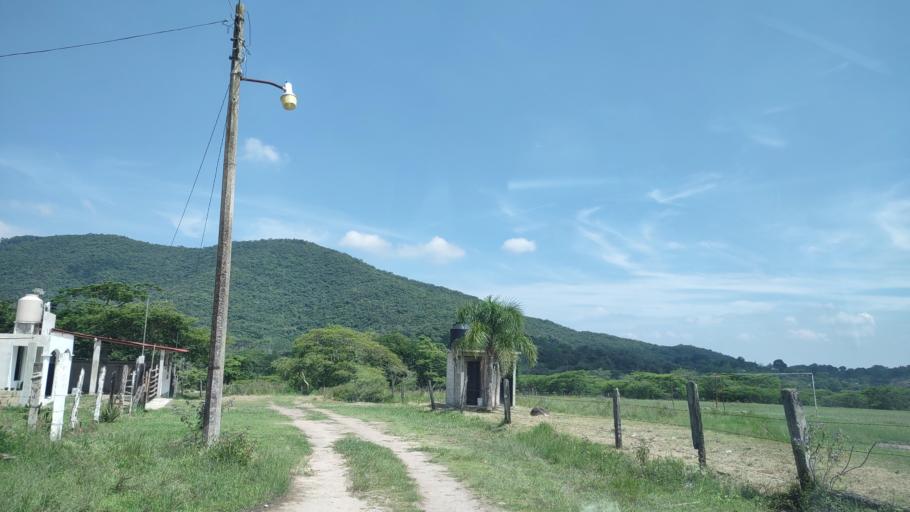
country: MX
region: Veracruz
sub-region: Coatepec
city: Bella Esperanza
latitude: 19.4273
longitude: -96.8098
